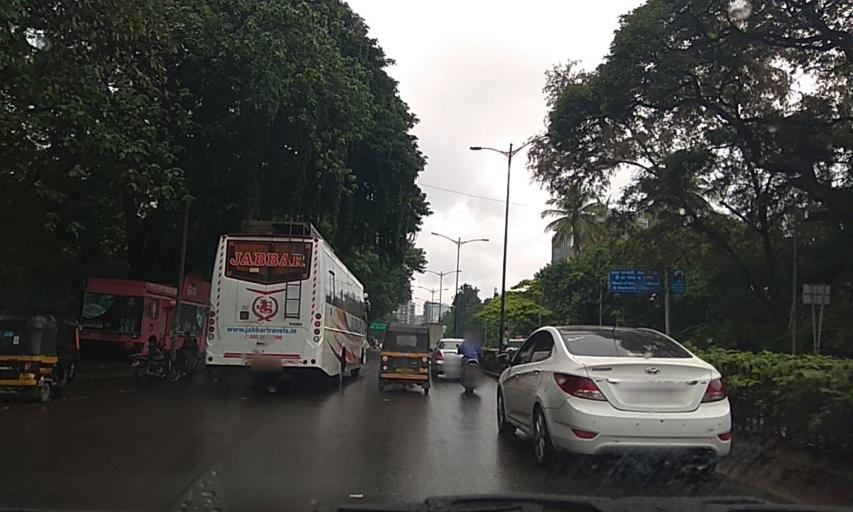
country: IN
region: Maharashtra
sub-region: Pune Division
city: Shivaji Nagar
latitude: 18.5303
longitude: 73.8489
